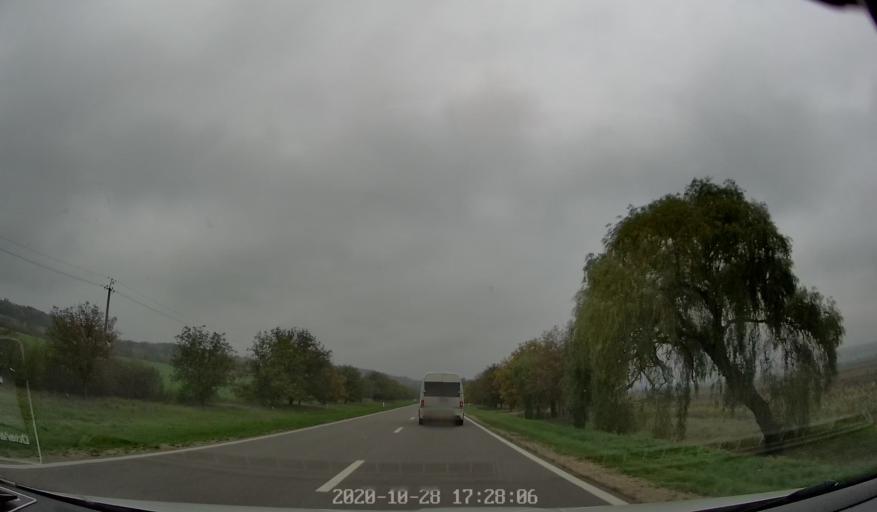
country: MD
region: Cimislia
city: Cimislia
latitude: 46.6568
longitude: 28.7028
